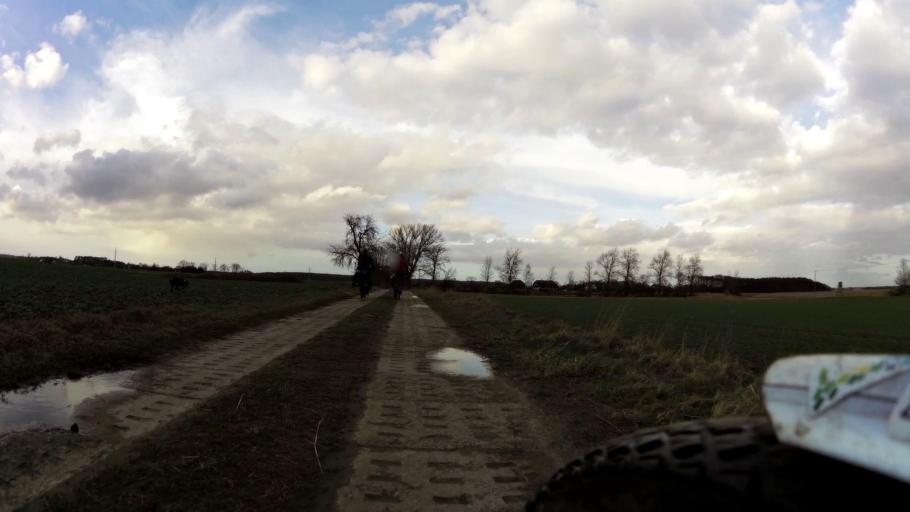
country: PL
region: West Pomeranian Voivodeship
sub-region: Powiat kamienski
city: Kamien Pomorski
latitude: 53.8900
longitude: 14.7196
